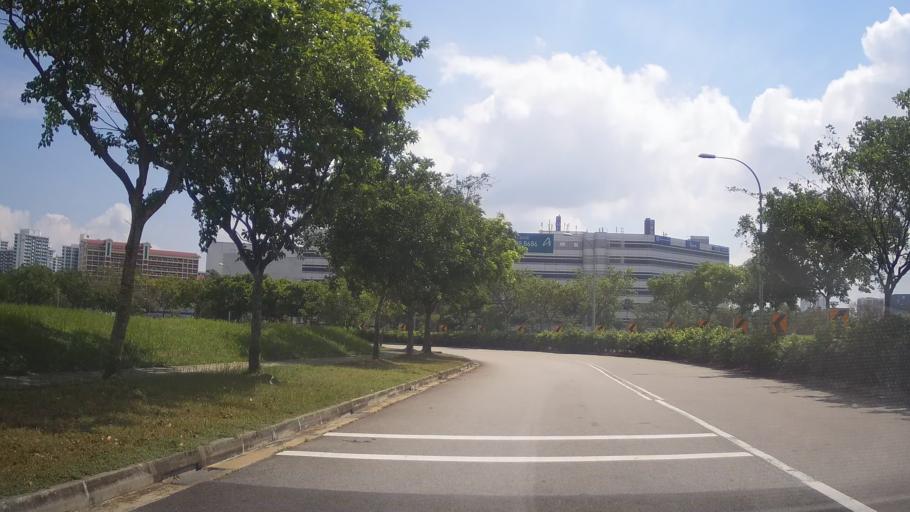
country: SG
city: Singapore
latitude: 1.3243
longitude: 103.7174
